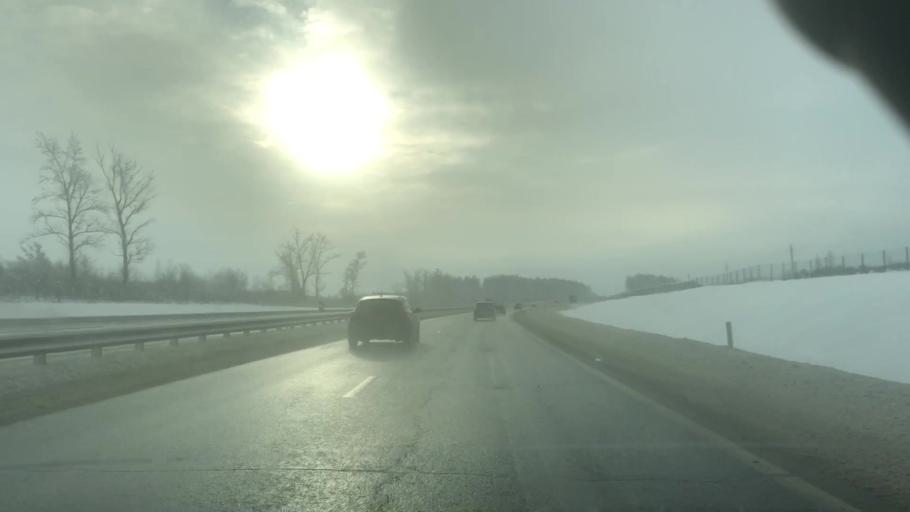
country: RU
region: Tula
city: Venev
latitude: 54.2735
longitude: 38.1602
